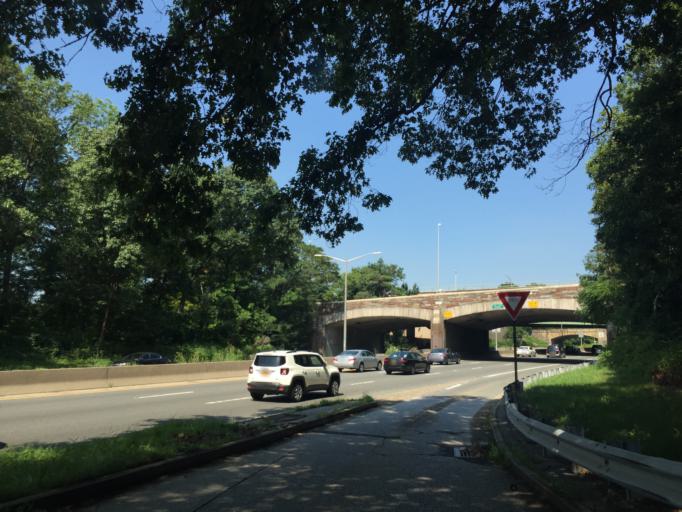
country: US
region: New York
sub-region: Nassau County
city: Bellerose Terrace
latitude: 40.7433
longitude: -73.7310
